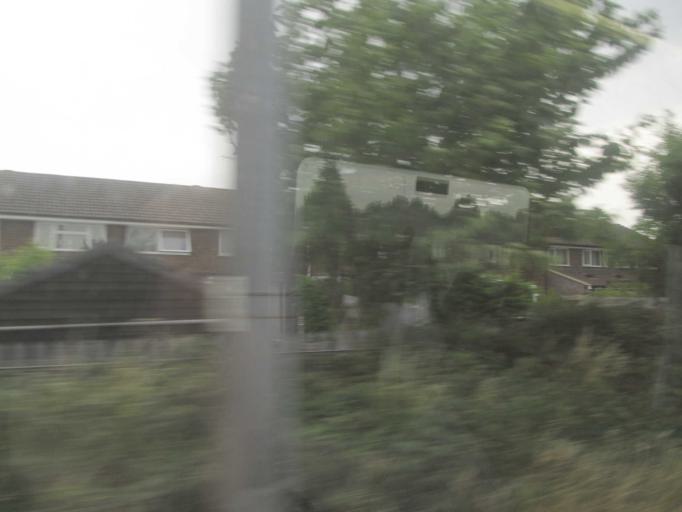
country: GB
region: England
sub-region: Bedford
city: Elstow
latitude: 52.1168
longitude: -0.4791
